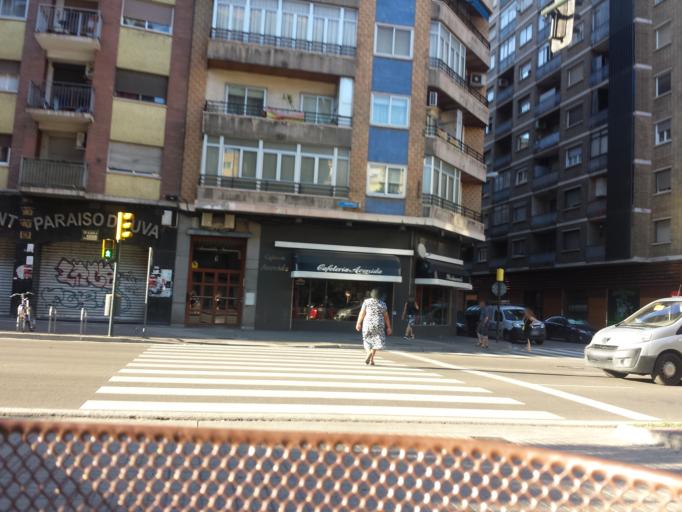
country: ES
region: Aragon
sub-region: Provincia de Zaragoza
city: Almozara
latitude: 41.6547
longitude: -0.9016
